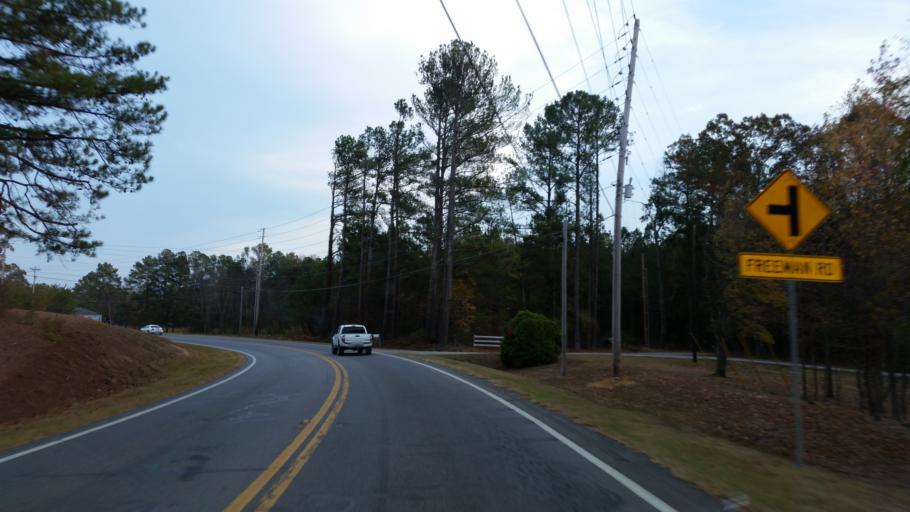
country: US
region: Georgia
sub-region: Gordon County
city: Calhoun
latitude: 34.5952
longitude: -84.9095
